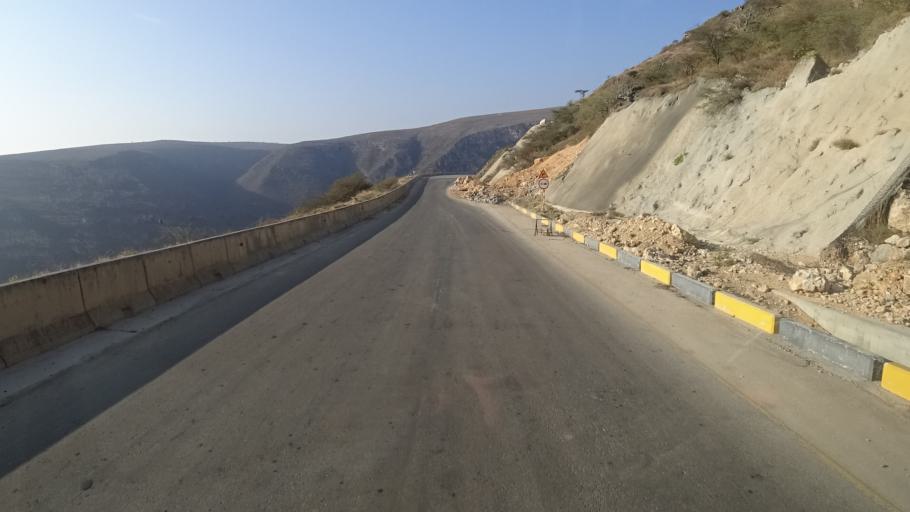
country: YE
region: Al Mahrah
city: Hawf
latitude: 16.7531
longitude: 53.2176
